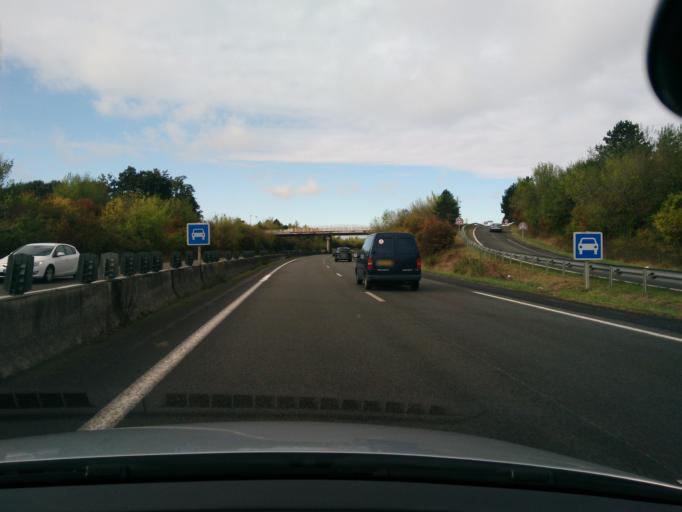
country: FR
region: Centre
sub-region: Departement d'Eure-et-Loir
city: Cherisy
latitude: 48.7495
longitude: 1.4327
